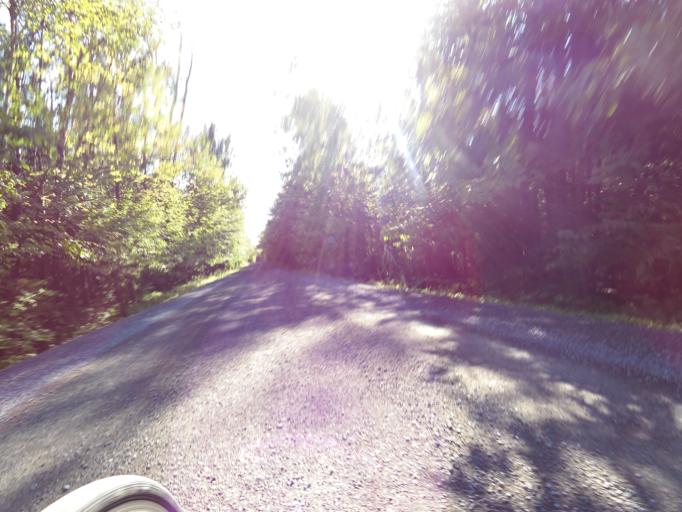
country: CA
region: Ontario
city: Bells Corners
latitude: 45.4823
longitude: -76.0423
